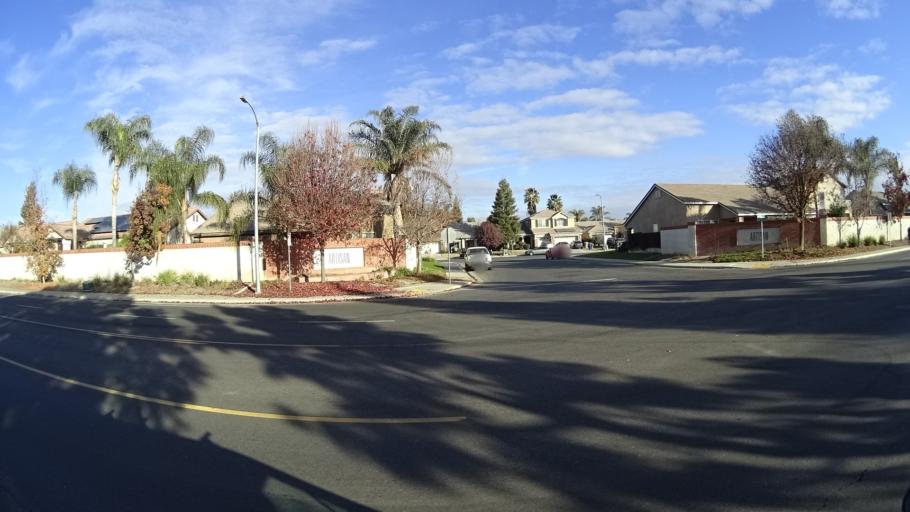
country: US
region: California
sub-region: Kern County
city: Greenacres
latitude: 35.3035
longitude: -119.1236
